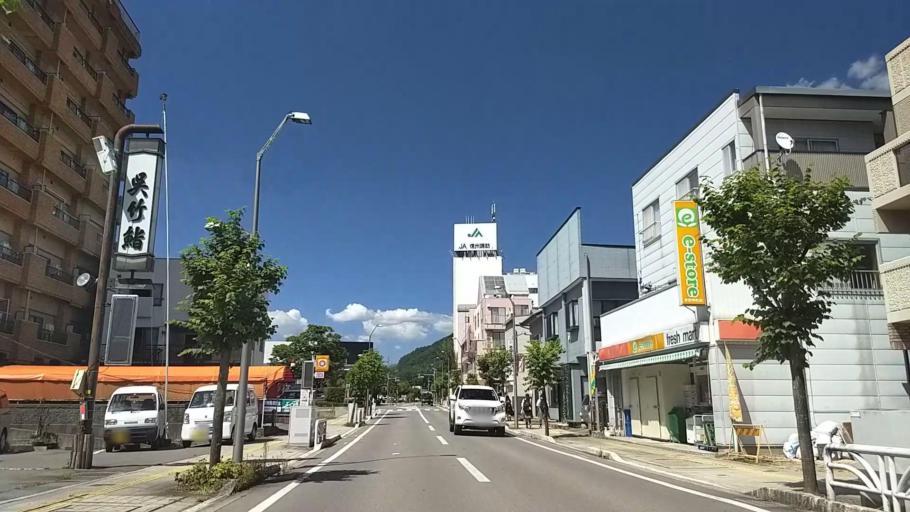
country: JP
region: Nagano
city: Chino
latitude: 35.9930
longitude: 138.1538
